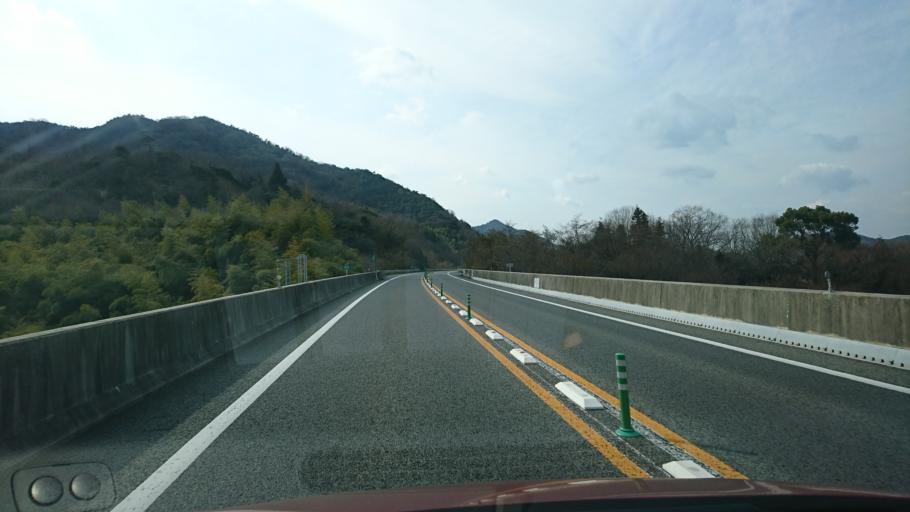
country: JP
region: Hiroshima
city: Innoshima
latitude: 34.1352
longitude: 133.0515
